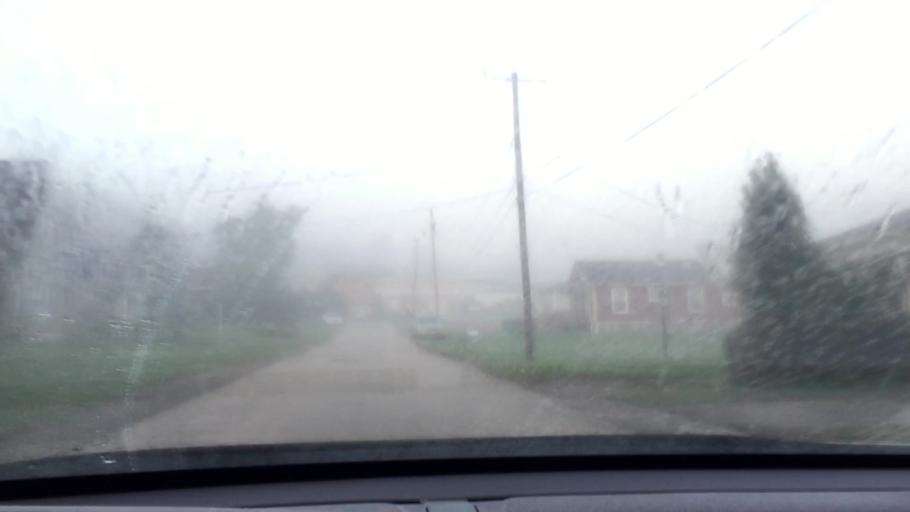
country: US
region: Pennsylvania
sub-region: Westmoreland County
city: Lynnwood-Pricedale
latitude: 40.1259
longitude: -79.8476
